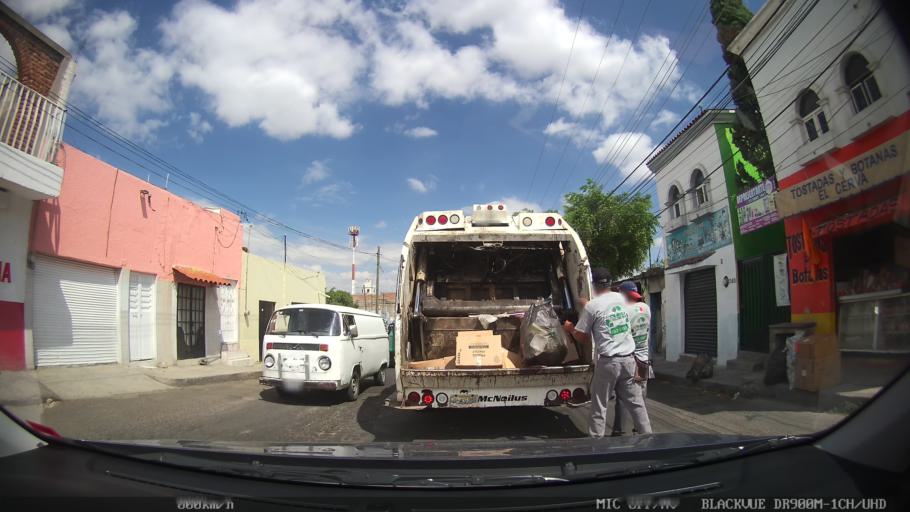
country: MX
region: Jalisco
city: Tonala
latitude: 20.6301
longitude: -103.2484
